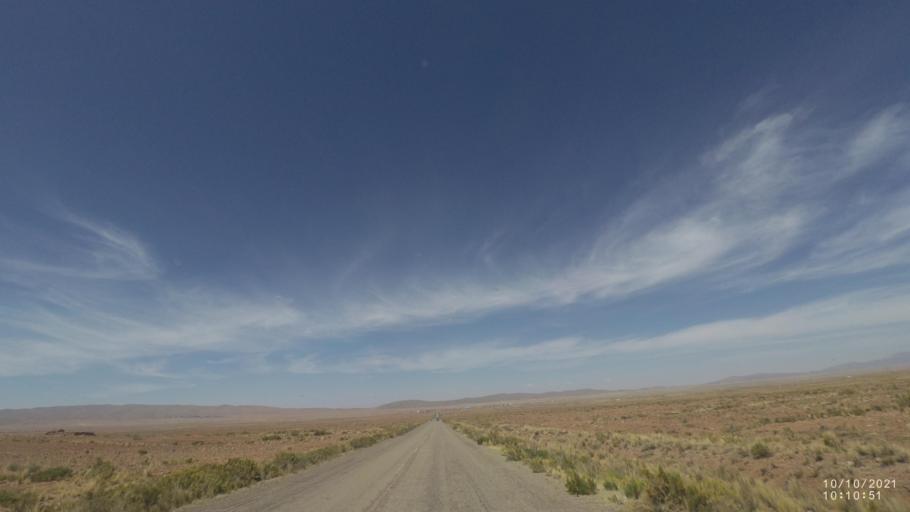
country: BO
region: La Paz
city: Eucaliptus
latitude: -17.4153
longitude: -67.4965
